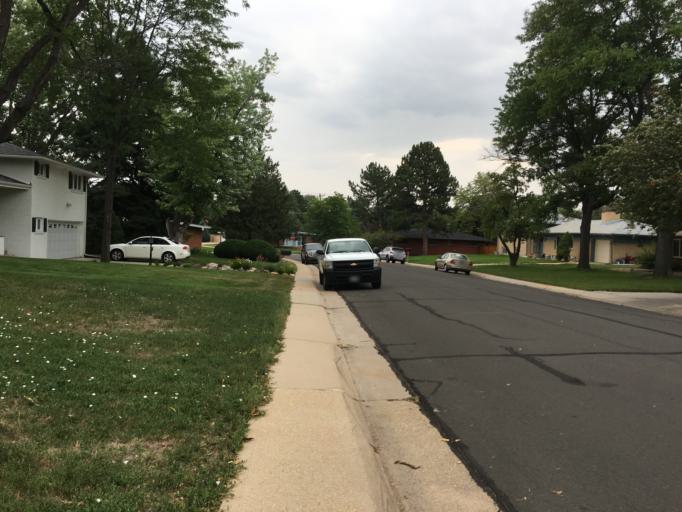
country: US
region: Colorado
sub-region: Arapahoe County
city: Glendale
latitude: 39.6716
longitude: -104.9234
